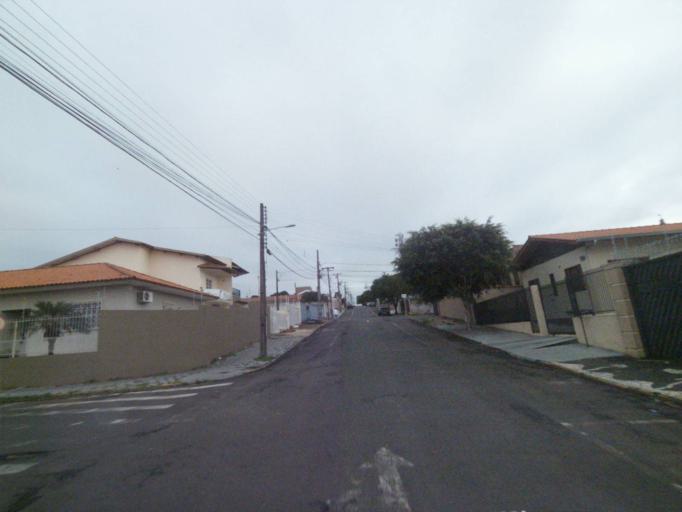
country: BR
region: Parana
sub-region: Telemaco Borba
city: Telemaco Borba
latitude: -24.3258
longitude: -50.6189
